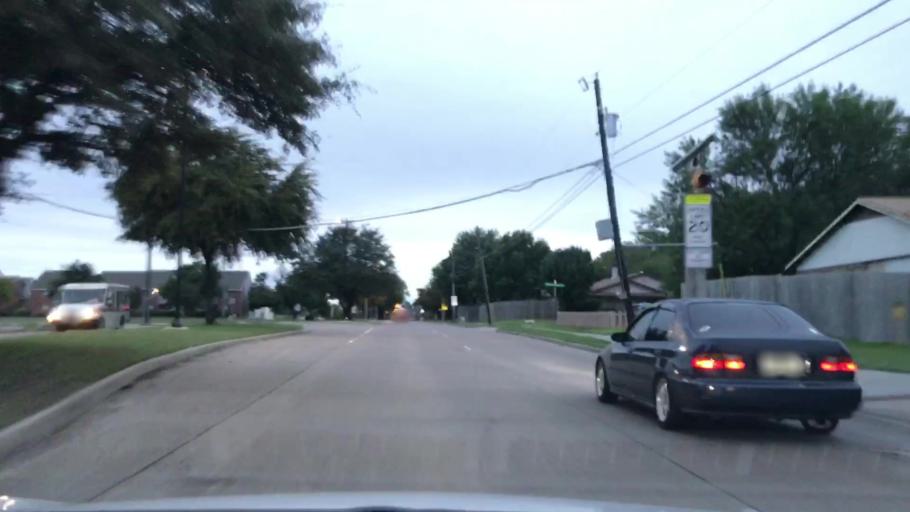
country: US
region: Texas
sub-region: Dallas County
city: Garland
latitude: 32.8446
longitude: -96.6213
